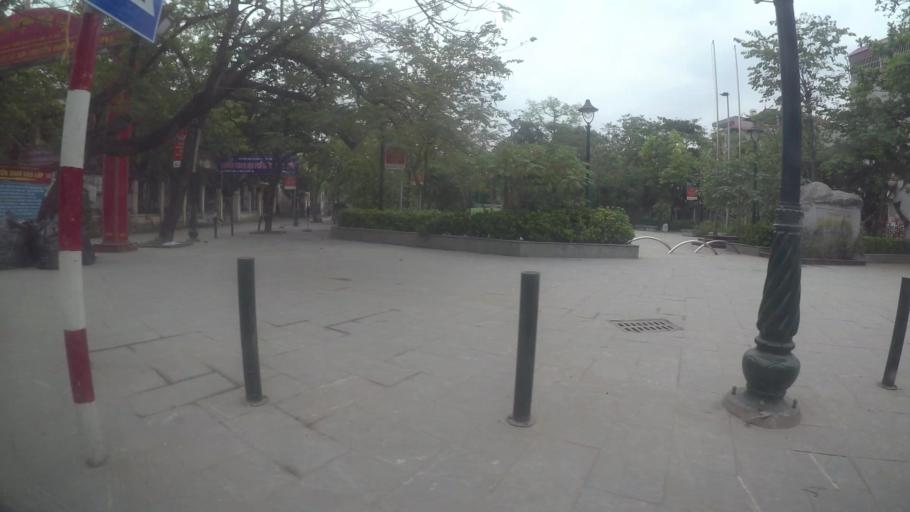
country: VN
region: Ha Noi
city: Cau Dien
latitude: 21.0349
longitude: 105.7400
